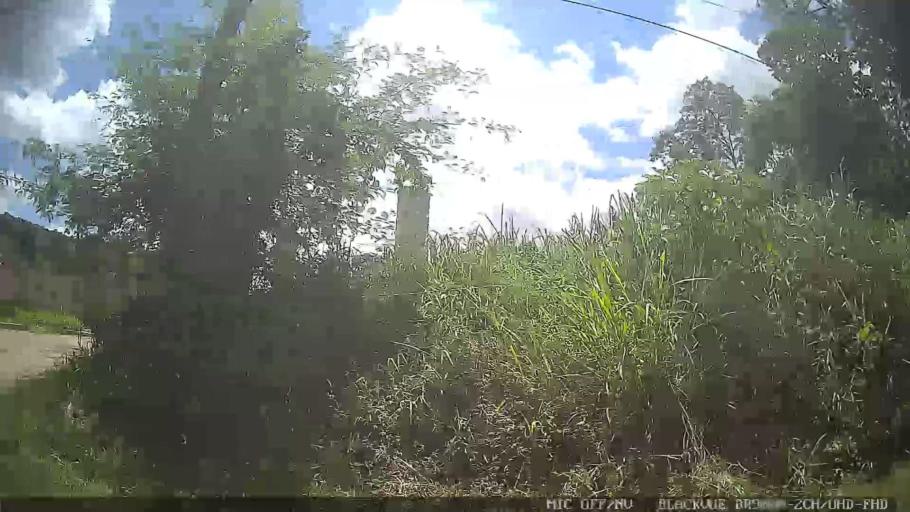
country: BR
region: Sao Paulo
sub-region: Atibaia
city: Atibaia
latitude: -23.0473
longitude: -46.5030
